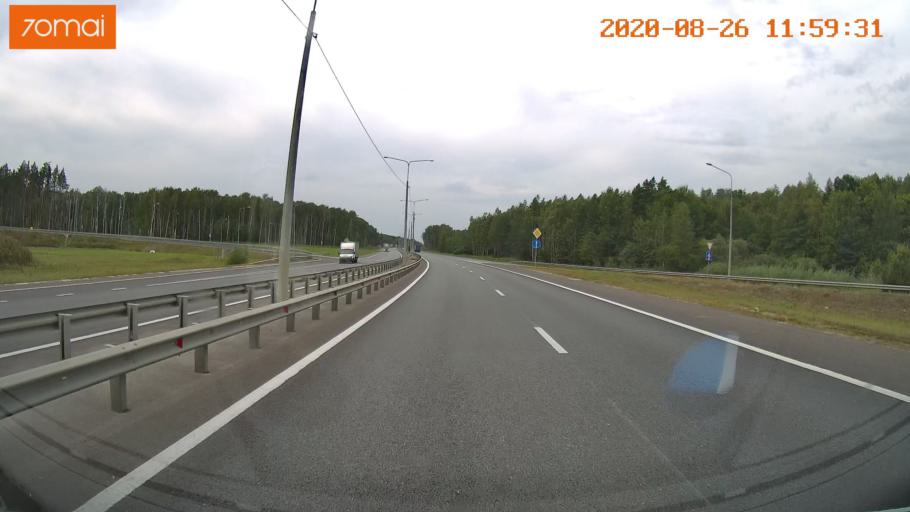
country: RU
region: Rjazan
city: Kiritsy
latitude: 54.2862
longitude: 40.2975
